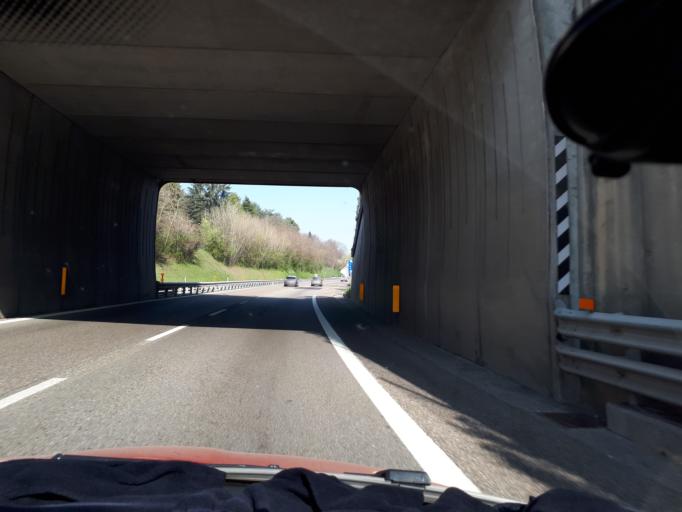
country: IT
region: Lombardy
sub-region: Provincia di Monza e Brianza
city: Lentate sul Seveso
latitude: 45.6751
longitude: 9.1102
